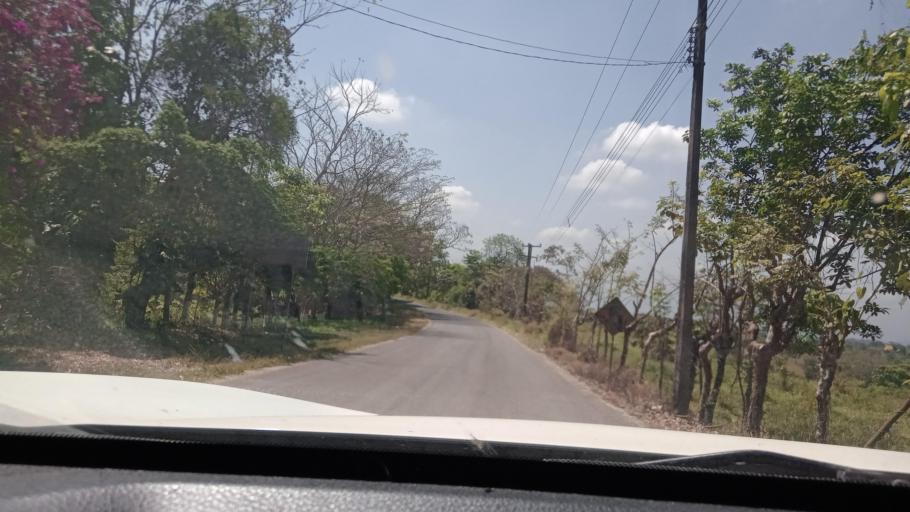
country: MX
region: Veracruz
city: Las Choapas
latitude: 17.7527
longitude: -94.1128
